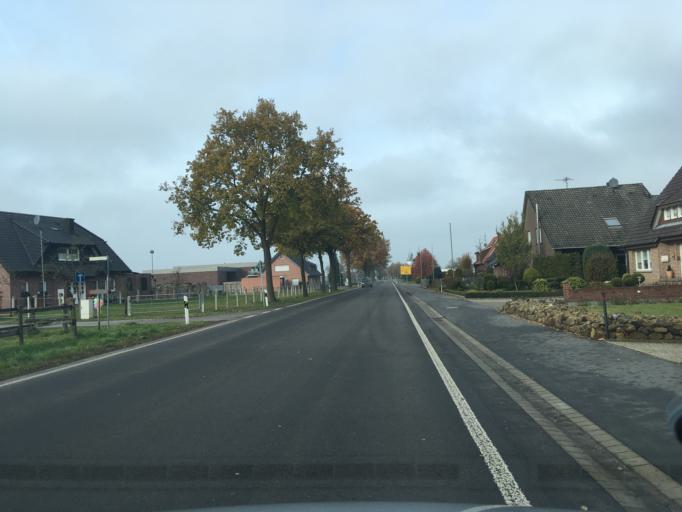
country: DE
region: North Rhine-Westphalia
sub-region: Regierungsbezirk Munster
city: Sudlohn
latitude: 51.9332
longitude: 6.8778
